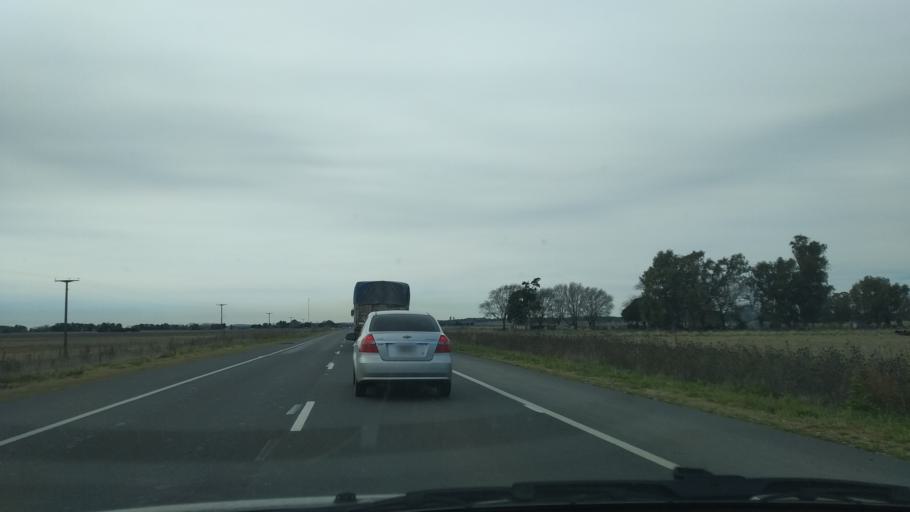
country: AR
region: Buenos Aires
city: Olavarria
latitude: -36.9972
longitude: -60.3389
